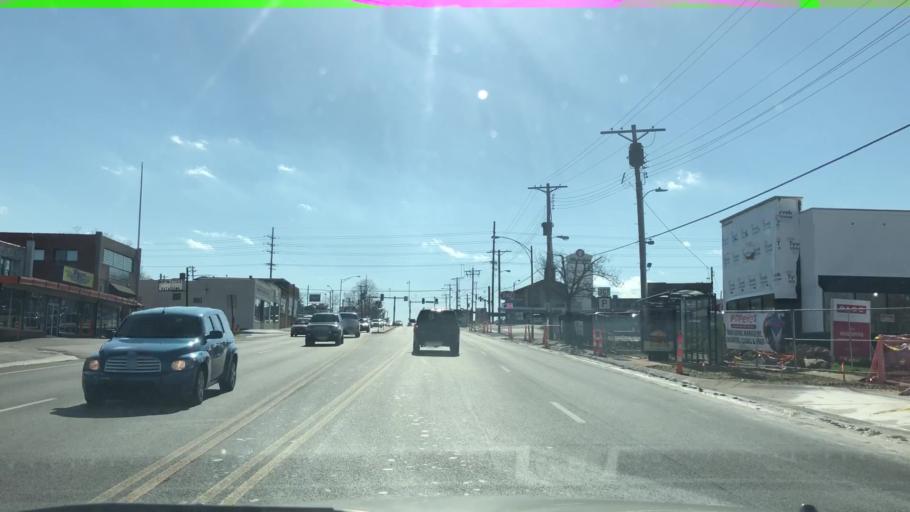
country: US
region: Missouri
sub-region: Saint Louis County
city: Affton
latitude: 38.5532
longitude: -90.3214
